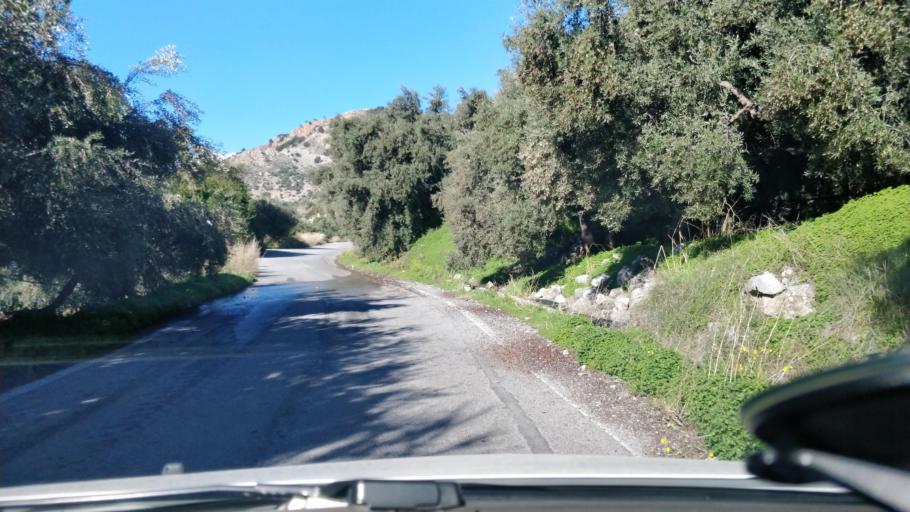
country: GR
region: Crete
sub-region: Nomos Lasithiou
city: Kritsa
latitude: 35.0770
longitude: 25.5844
